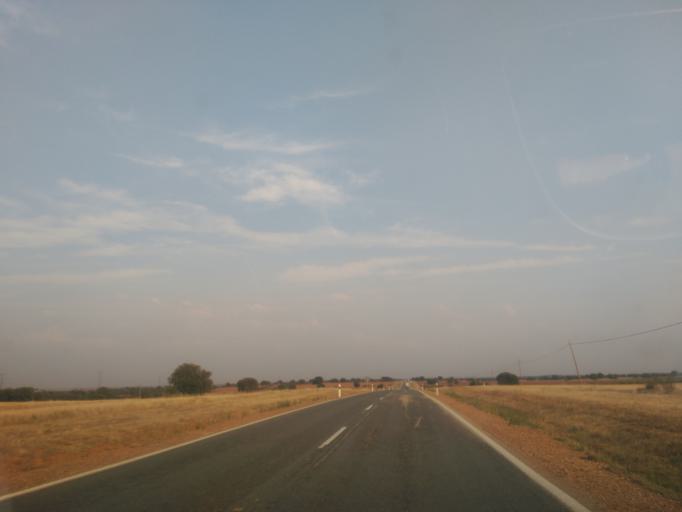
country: ES
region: Castille and Leon
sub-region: Provincia de Zamora
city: Perilla de Castro
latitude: 41.7419
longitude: -5.8350
